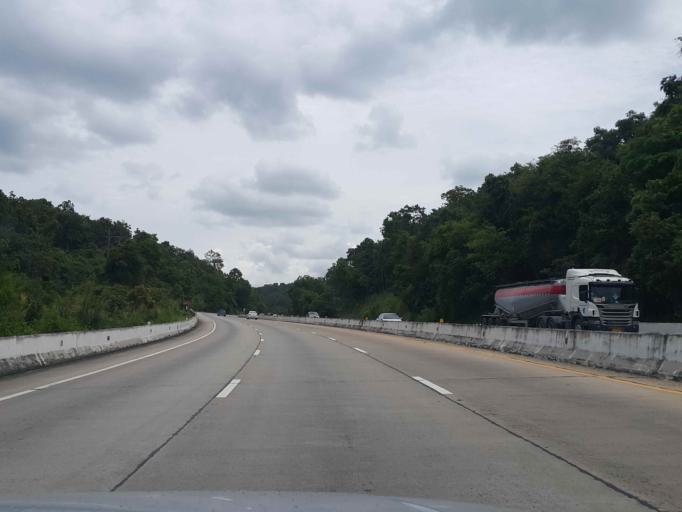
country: TH
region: Lamphun
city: Mae Tha
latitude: 18.4418
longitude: 99.2049
